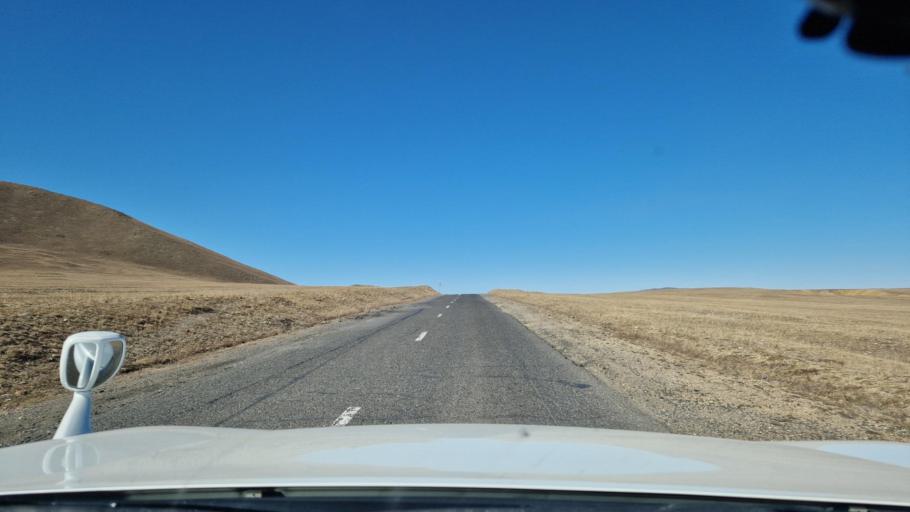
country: MN
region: Hentiy
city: Modot
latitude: 47.7516
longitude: 108.9598
